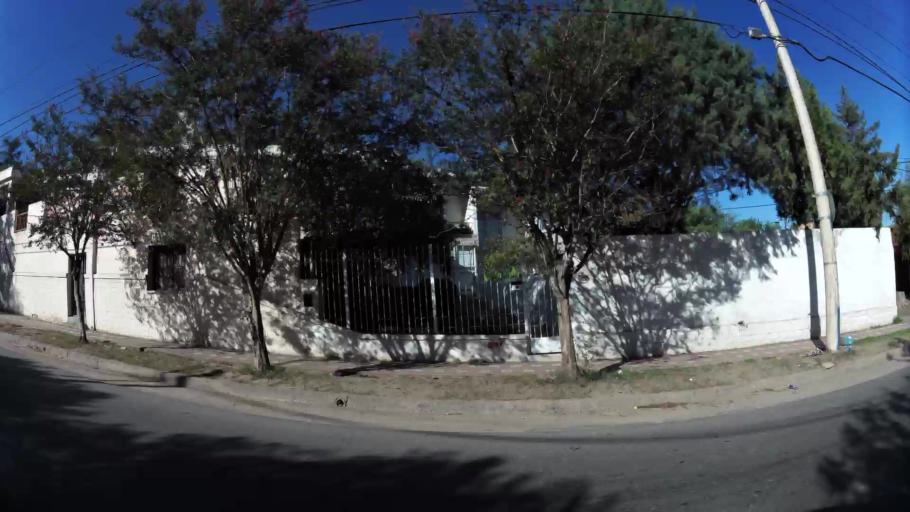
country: AR
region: Cordoba
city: Villa Allende
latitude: -31.3655
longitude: -64.2524
